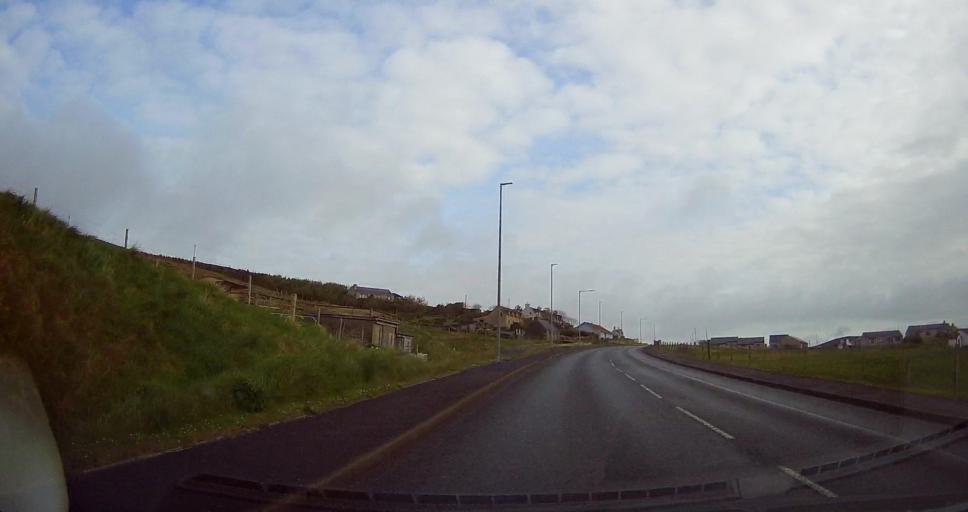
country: GB
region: Scotland
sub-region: Shetland Islands
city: Sandwick
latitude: 60.0428
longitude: -1.2293
